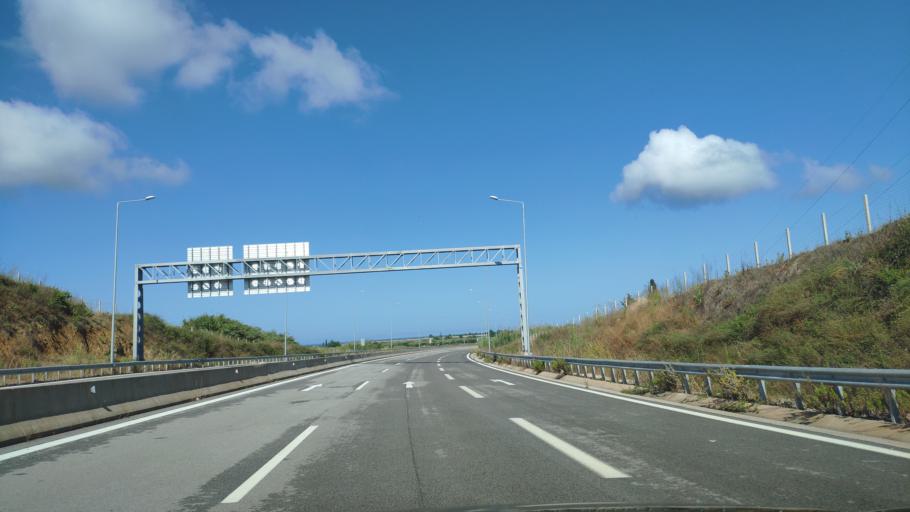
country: GR
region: Epirus
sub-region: Nomos Prevezis
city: Preveza
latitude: 38.9128
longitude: 20.8031
